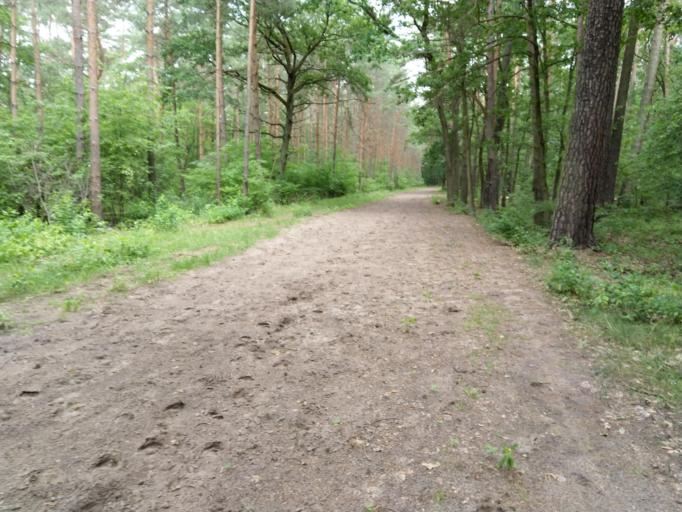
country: DE
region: Berlin
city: Friedrichshagen
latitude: 52.4759
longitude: 13.6475
